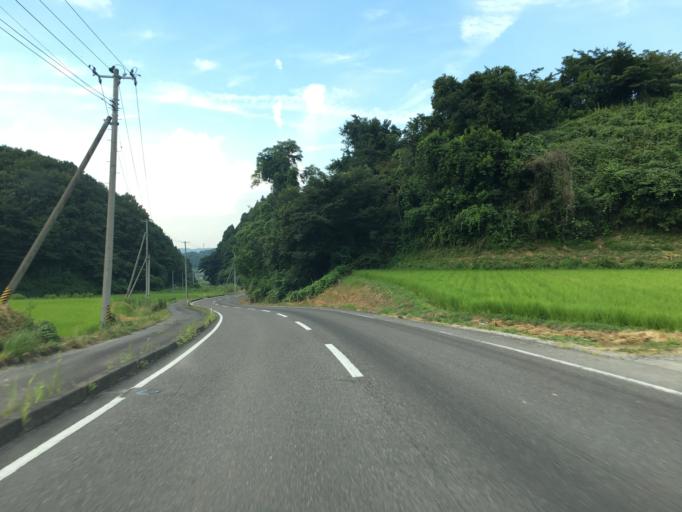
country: JP
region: Fukushima
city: Motomiya
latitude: 37.5369
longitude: 140.4418
